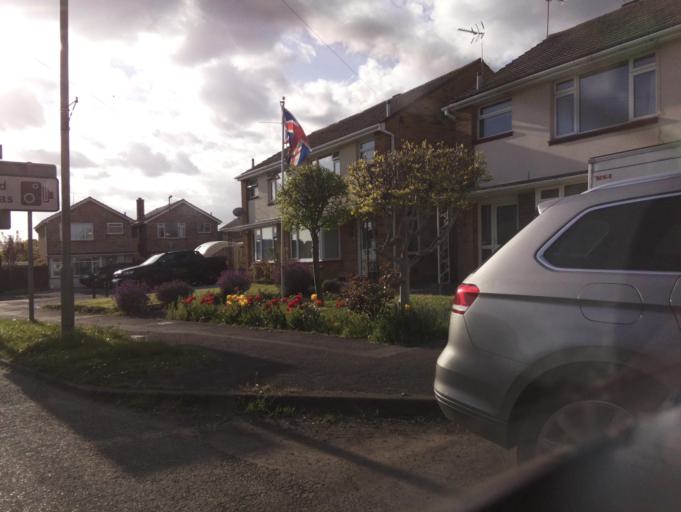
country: GB
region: England
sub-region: Hampshire
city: Bishopstoke
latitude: 50.9635
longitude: -1.2977
